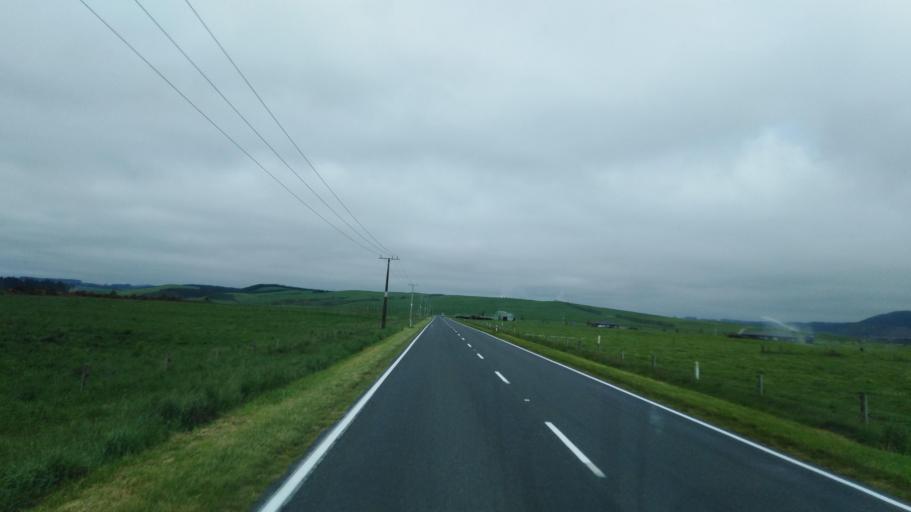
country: NZ
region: Waikato
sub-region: Taupo District
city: Taupo
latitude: -38.6162
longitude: 176.2427
